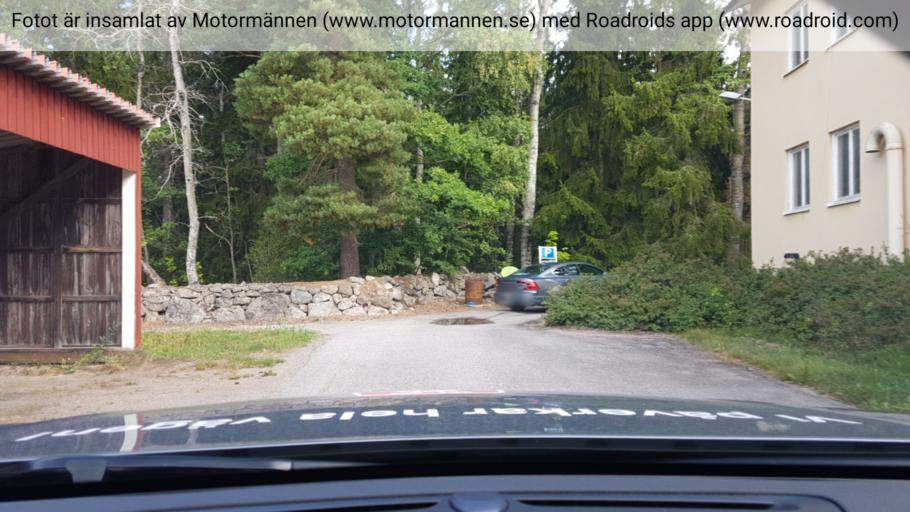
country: SE
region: Uppsala
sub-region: Heby Kommun
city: Tarnsjo
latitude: 60.2889
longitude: 16.8967
